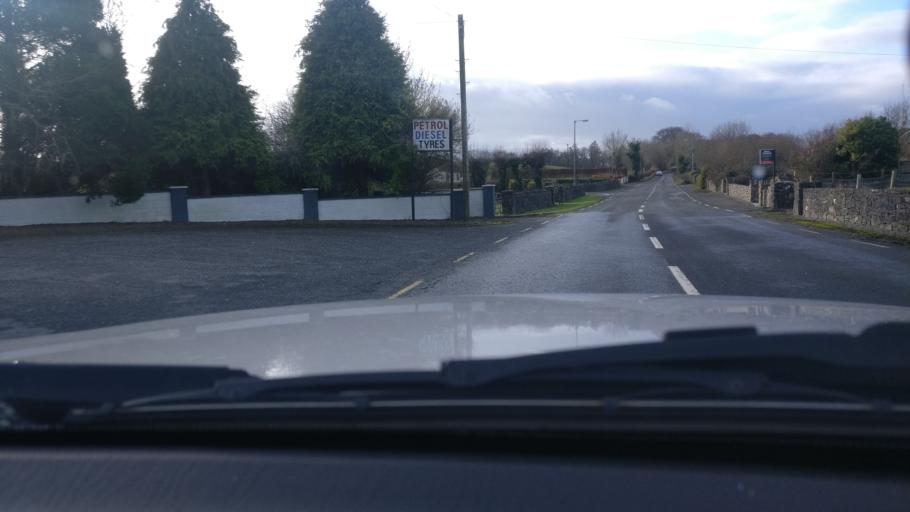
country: IE
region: Connaught
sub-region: County Galway
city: Ballinasloe
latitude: 53.2339
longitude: -8.2782
